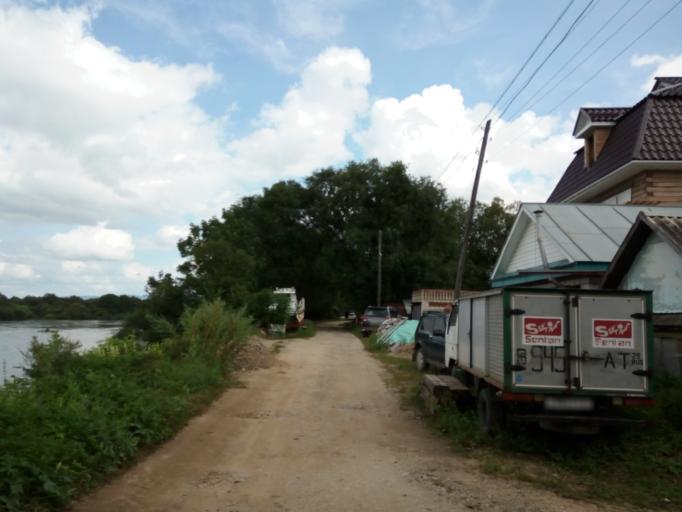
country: RU
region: Primorskiy
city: Dal'nerechensk
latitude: 45.9566
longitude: 133.8187
